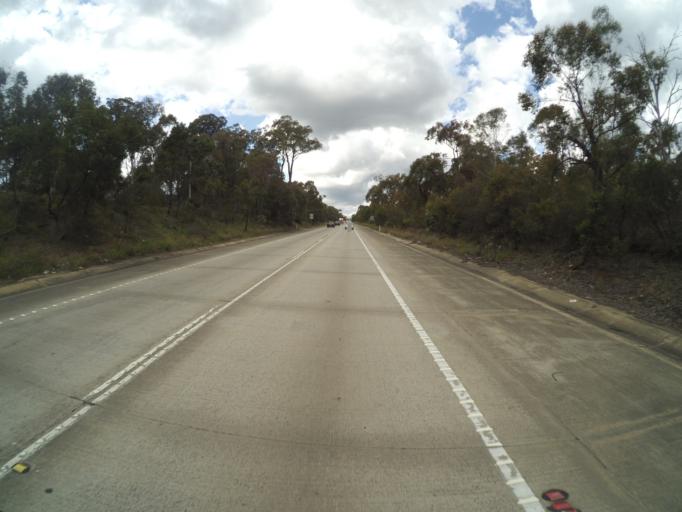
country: AU
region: New South Wales
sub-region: Wollondilly
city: Douglas Park
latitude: -34.2566
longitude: 150.7063
